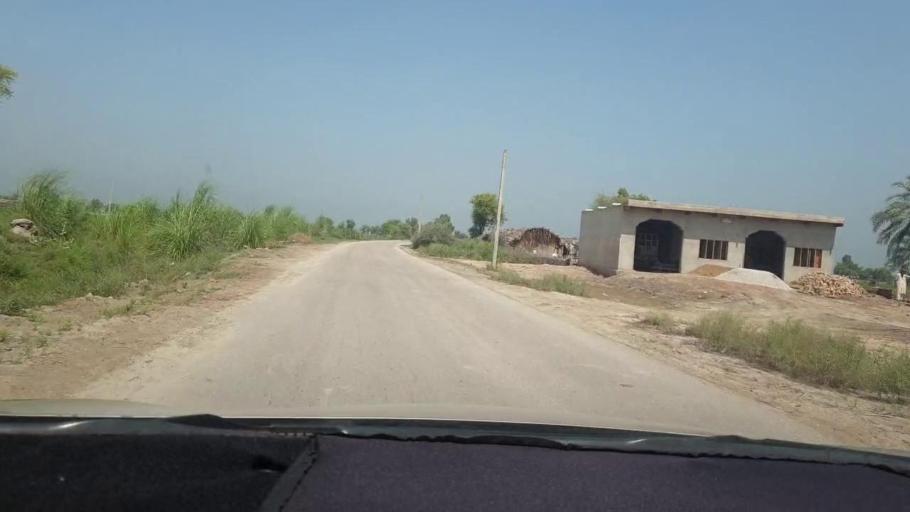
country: PK
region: Sindh
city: Miro Khan
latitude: 27.8179
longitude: 68.0252
